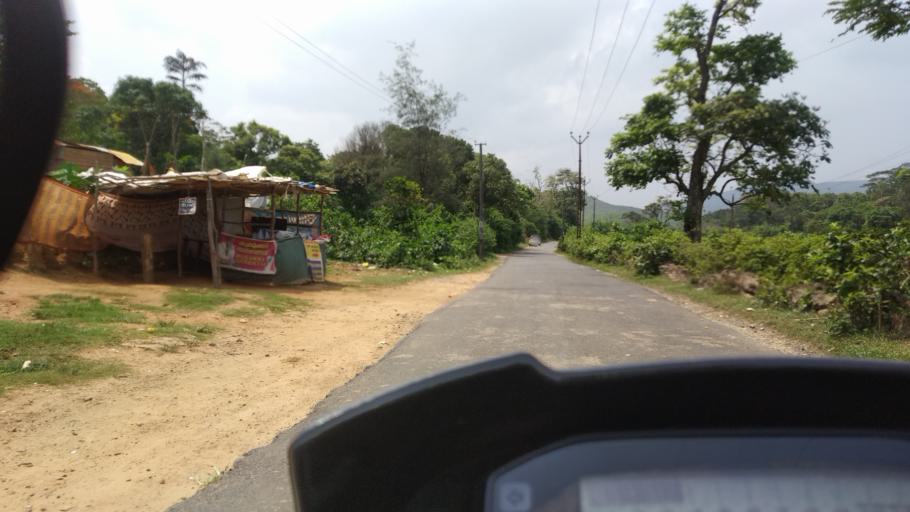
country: IN
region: Kerala
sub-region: Kottayam
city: Erattupetta
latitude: 9.6396
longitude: 76.9295
